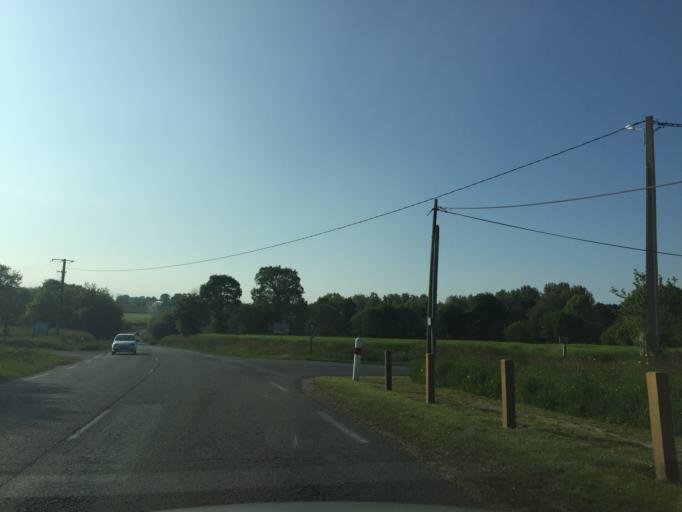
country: FR
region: Brittany
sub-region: Departement des Cotes-d'Armor
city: Crehen
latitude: 48.5855
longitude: -2.2382
